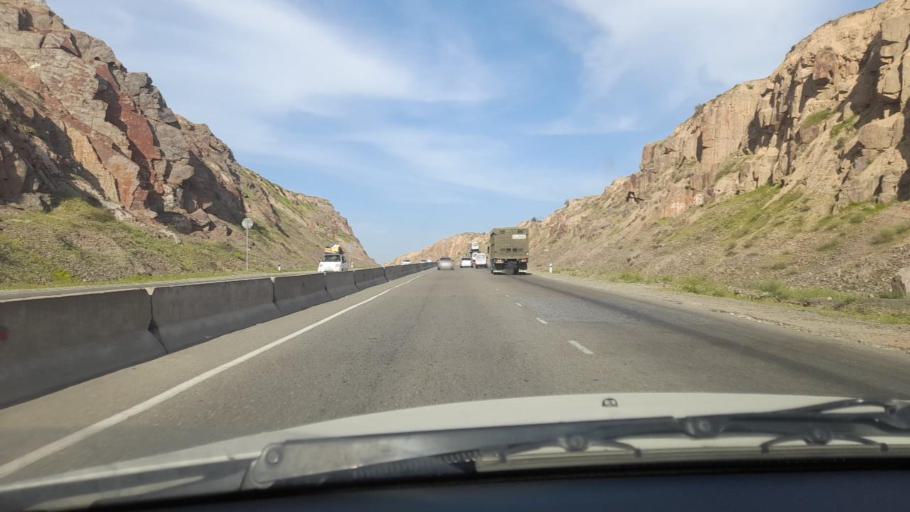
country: UZ
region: Jizzax
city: Jizzax
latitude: 40.0390
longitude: 67.6466
